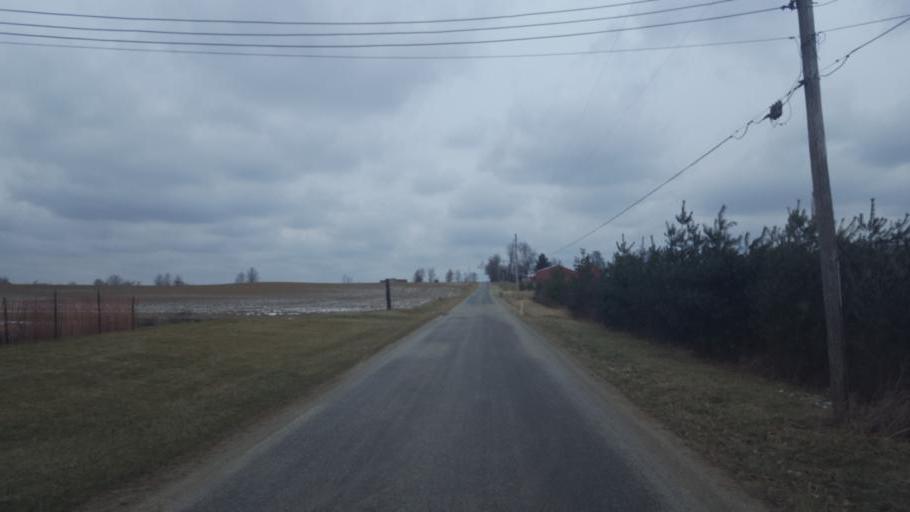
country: US
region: Ohio
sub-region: Crawford County
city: Crestline
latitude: 40.7242
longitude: -82.7034
